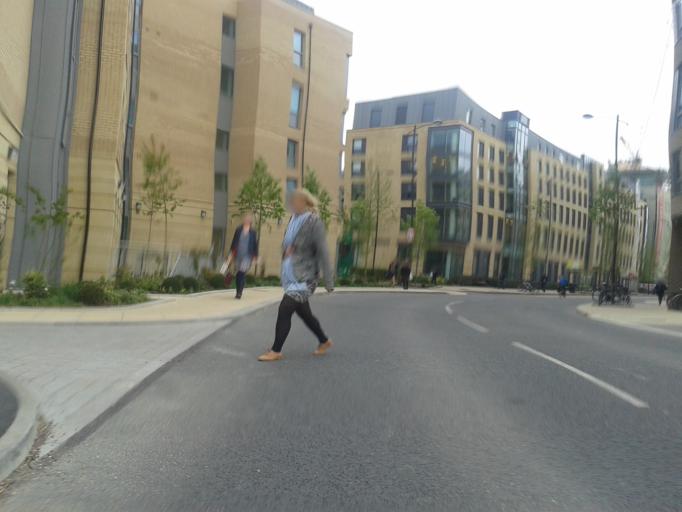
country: GB
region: England
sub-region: Cambridgeshire
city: Cambridge
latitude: 52.1919
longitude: 0.1355
